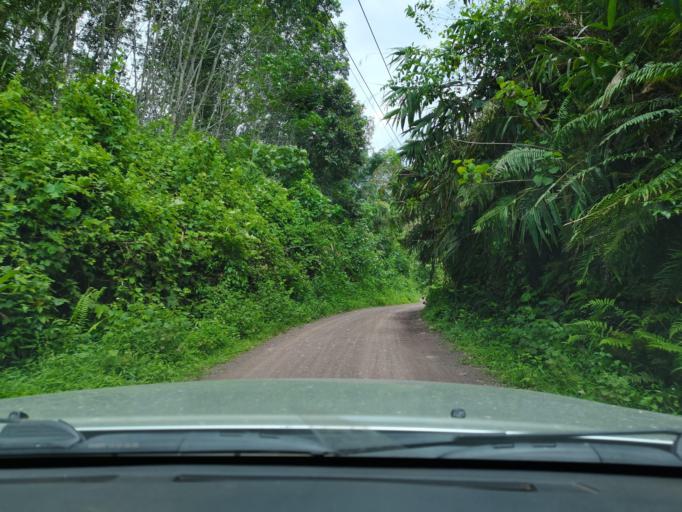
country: LA
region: Loungnamtha
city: Muang Long
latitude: 20.7008
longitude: 101.0262
